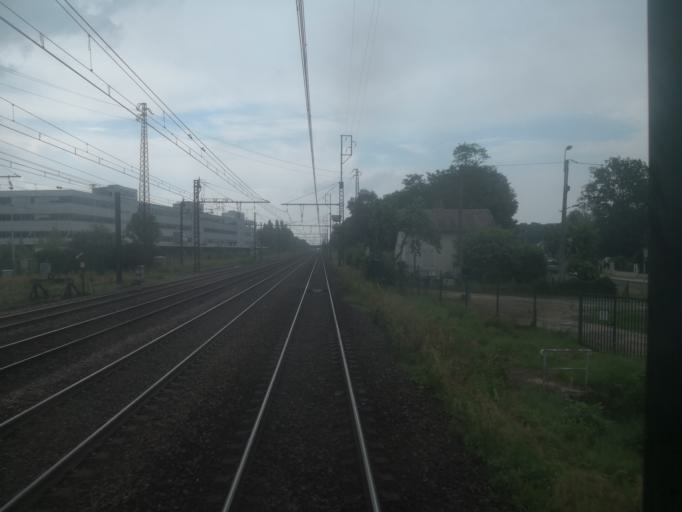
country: FR
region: Centre
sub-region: Departement du Loiret
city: Saran
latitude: 47.9493
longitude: 1.8959
